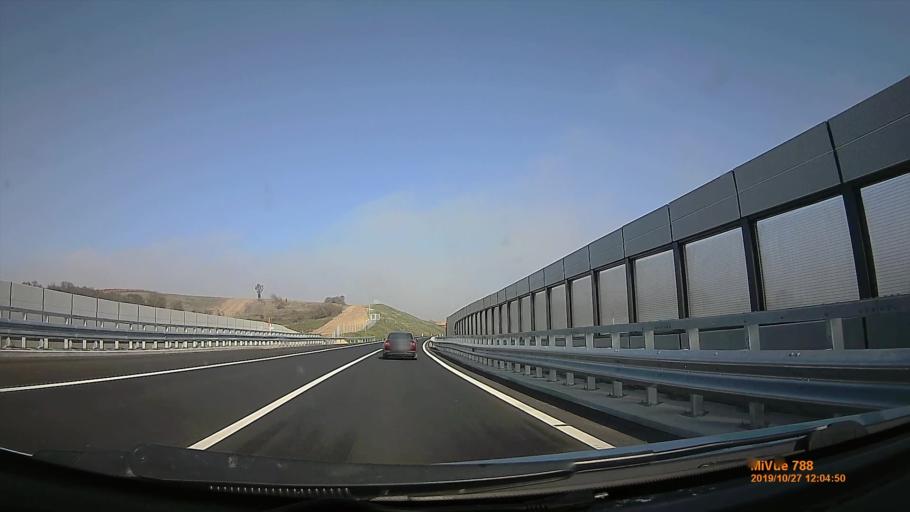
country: AT
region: Lower Austria
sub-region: Politischer Bezirk Mistelbach
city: Drasenhofen
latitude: 48.7569
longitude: 16.6338
